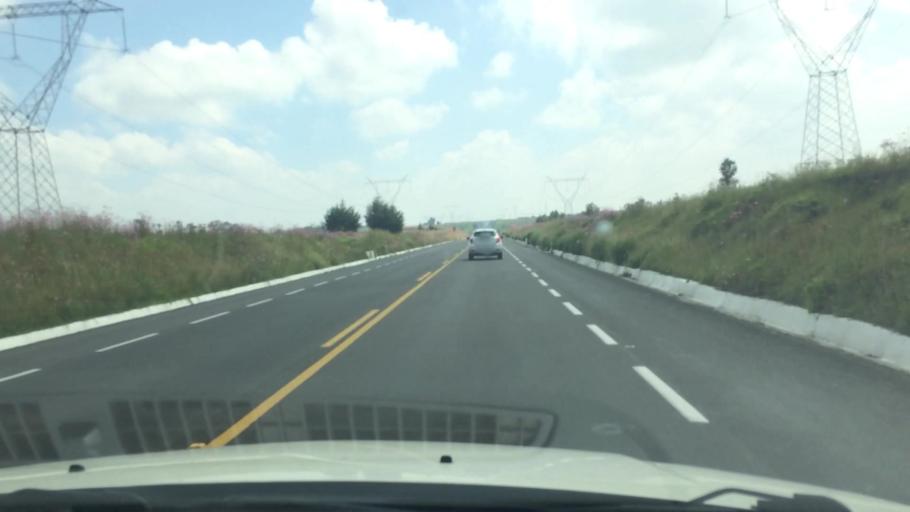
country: MX
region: Mexico
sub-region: Almoloya de Juarez
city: San Pedro de la Hortaliza (Ejido Almoloyan)
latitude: 19.3793
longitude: -99.8269
